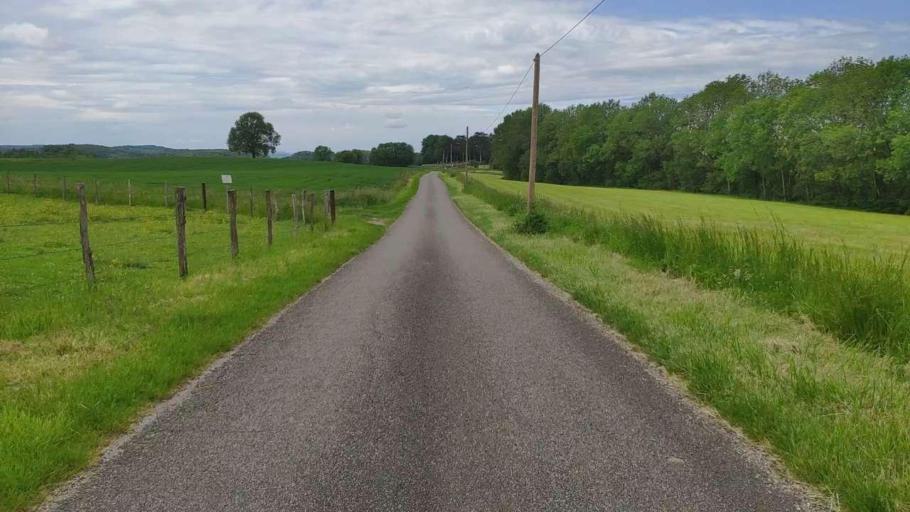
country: FR
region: Franche-Comte
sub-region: Departement du Jura
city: Perrigny
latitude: 46.7585
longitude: 5.6352
